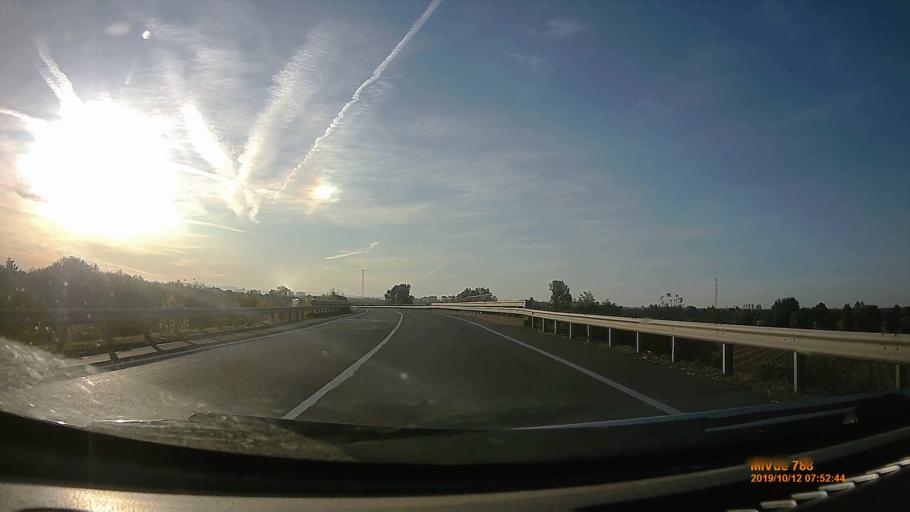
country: HU
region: Hajdu-Bihar
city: Biharkeresztes
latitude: 47.1329
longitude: 21.7419
